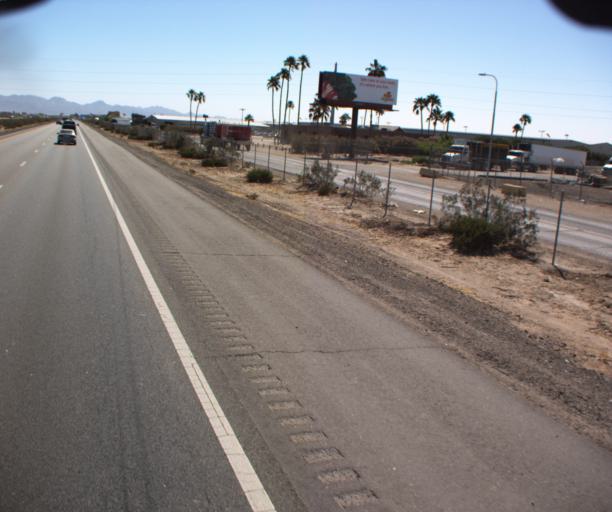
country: US
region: Arizona
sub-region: Yuma County
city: Yuma
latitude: 32.6818
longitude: -114.5564
